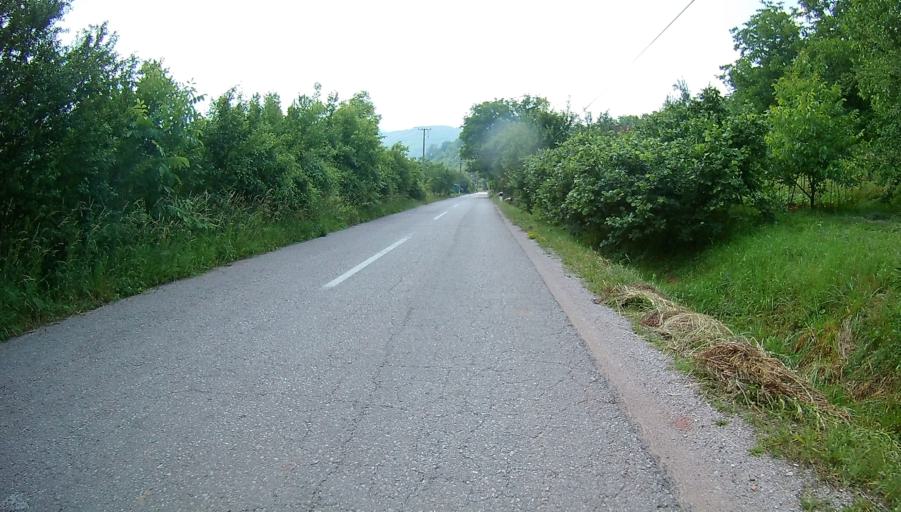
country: RS
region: Central Serbia
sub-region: Nisavski Okrug
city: Gadzin Han
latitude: 43.1748
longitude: 22.0599
